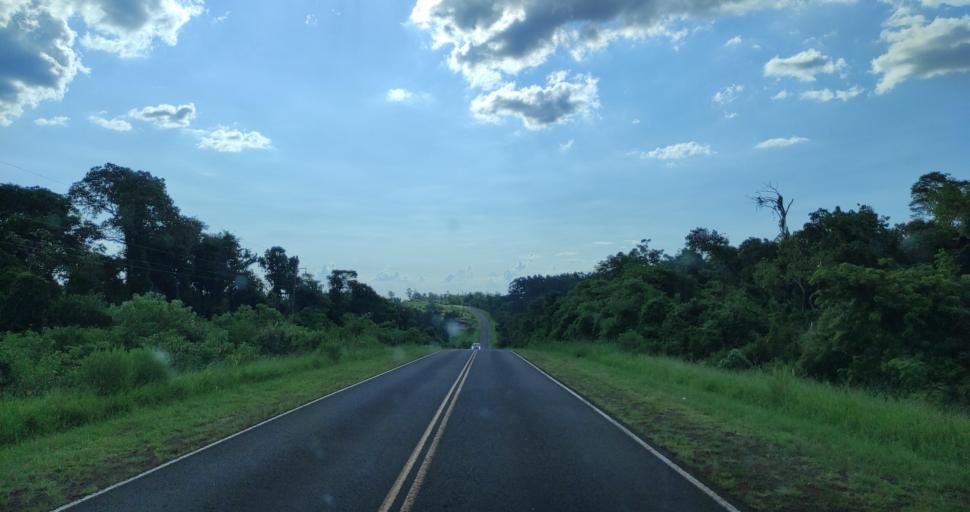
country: AR
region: Misiones
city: San Vicente
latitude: -26.3505
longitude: -54.1946
